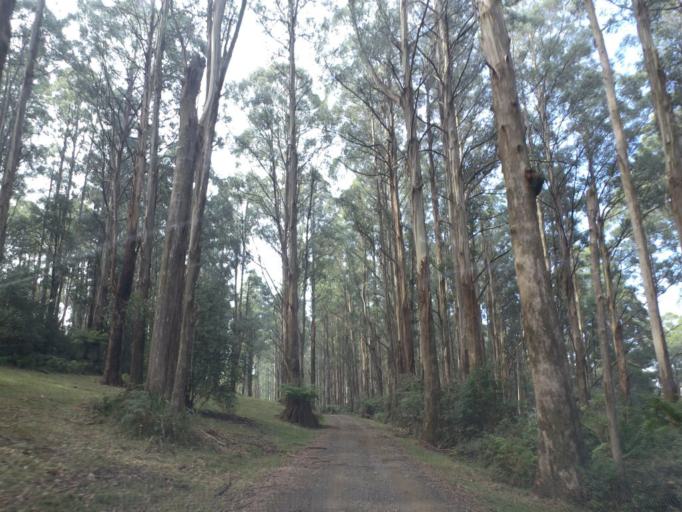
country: AU
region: Victoria
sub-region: Yarra Ranges
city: Healesville
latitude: -37.5875
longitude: 145.5552
